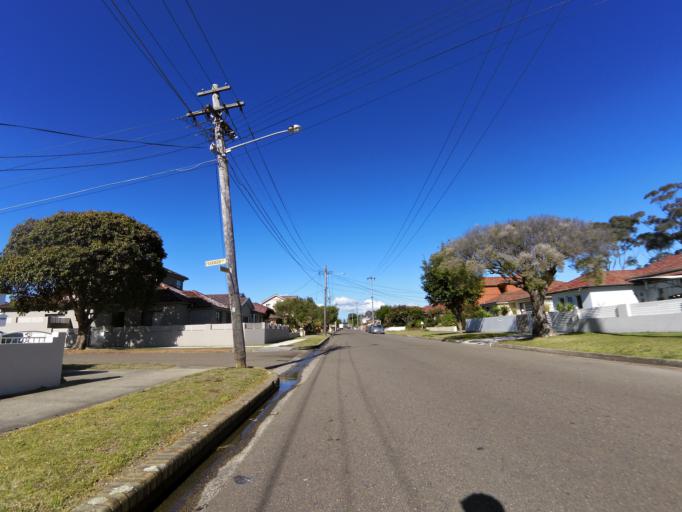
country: AU
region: New South Wales
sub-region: Rockdale
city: Brighton-Le-Sands
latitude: -33.9537
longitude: 151.1531
